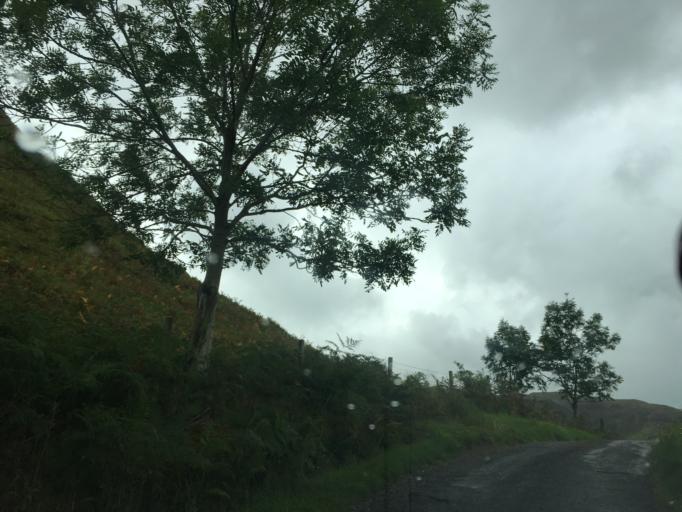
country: GB
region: Scotland
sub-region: Argyll and Bute
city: Oban
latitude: 56.2609
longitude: -5.4686
